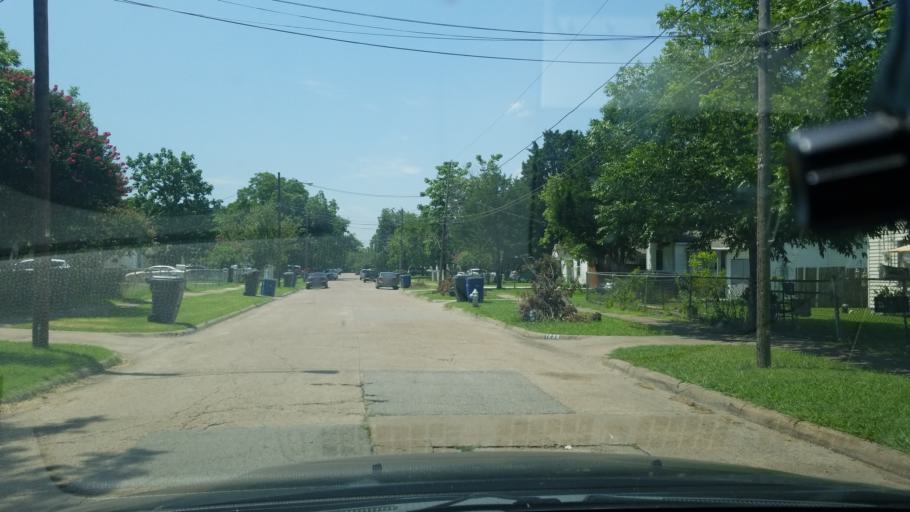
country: US
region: Texas
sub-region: Dallas County
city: Balch Springs
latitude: 32.7334
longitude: -96.6902
